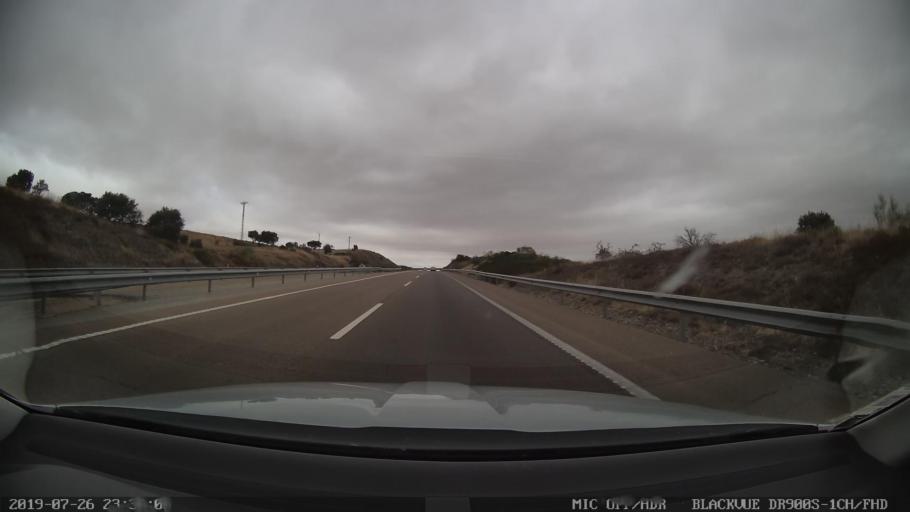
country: ES
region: Extremadura
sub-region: Provincia de Caceres
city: Santa Cruz de la Sierra
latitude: 39.3535
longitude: -5.8609
